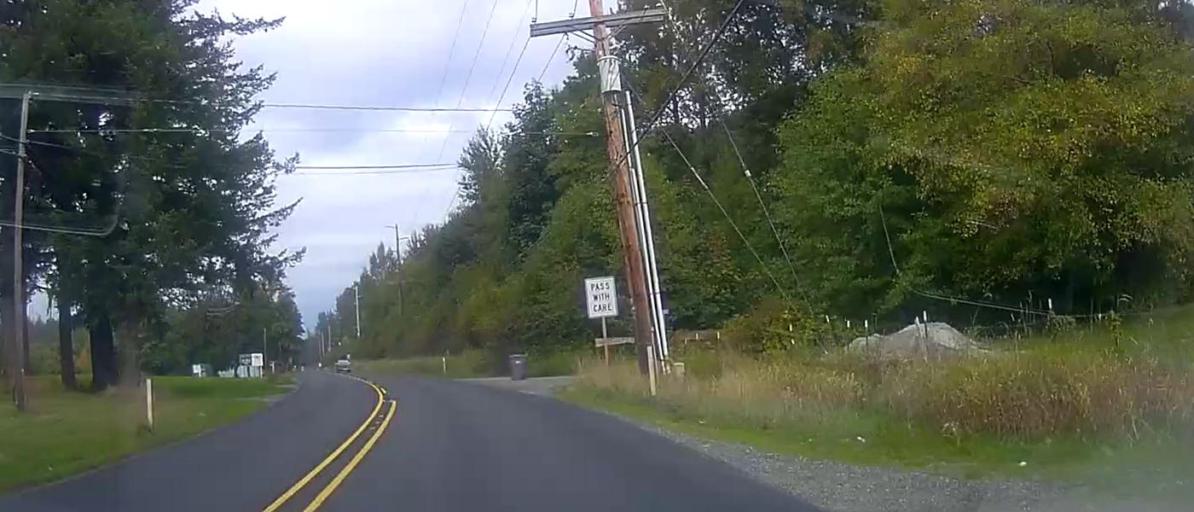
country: US
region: Washington
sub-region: Skagit County
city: Clear Lake
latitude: 48.4732
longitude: -122.2372
